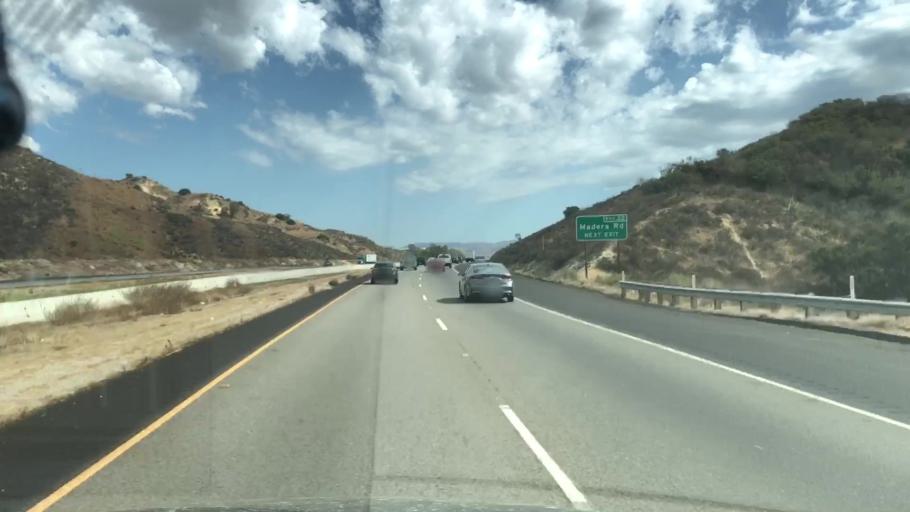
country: US
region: California
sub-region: Ventura County
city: Simi Valley
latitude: 34.2899
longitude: -118.8055
